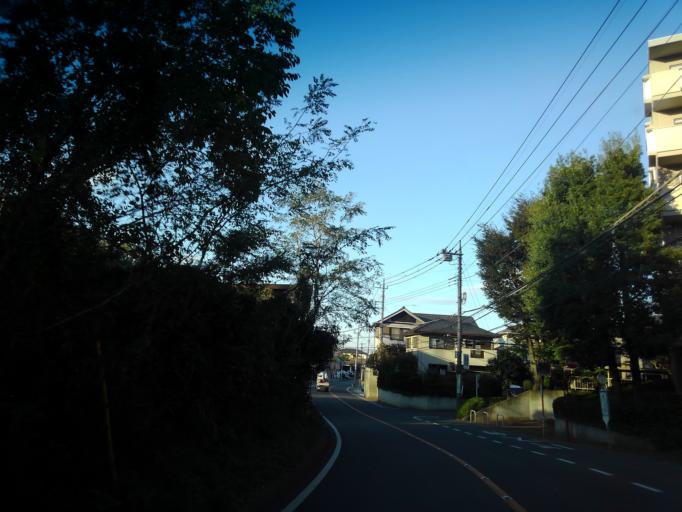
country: JP
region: Saitama
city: Tokorozawa
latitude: 35.7823
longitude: 139.4263
